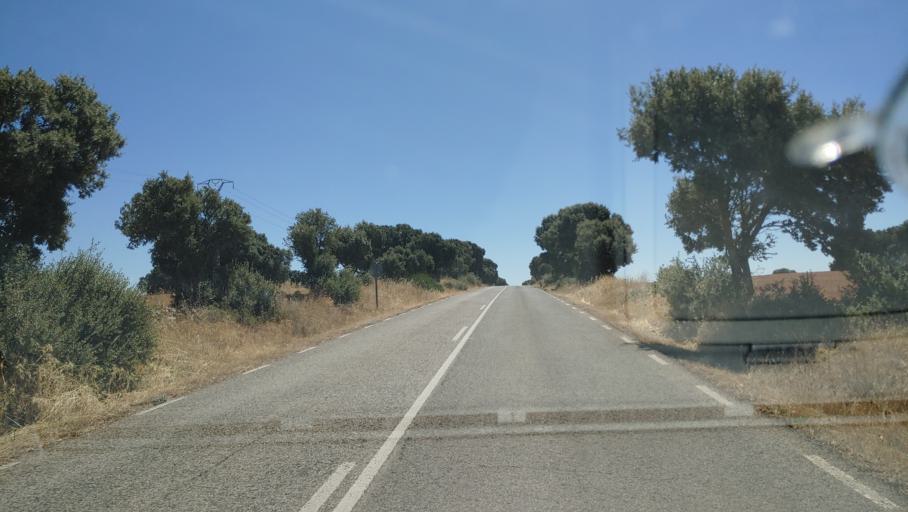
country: ES
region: Castille-La Mancha
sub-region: Provincia de Albacete
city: Ossa de Montiel
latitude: 38.9272
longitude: -2.7538
